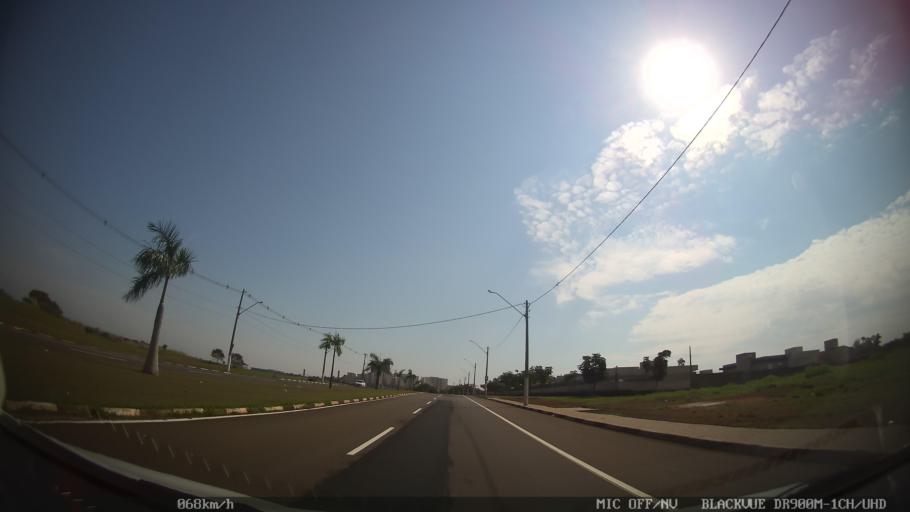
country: BR
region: Sao Paulo
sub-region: Paulinia
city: Paulinia
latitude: -22.7860
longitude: -47.1453
